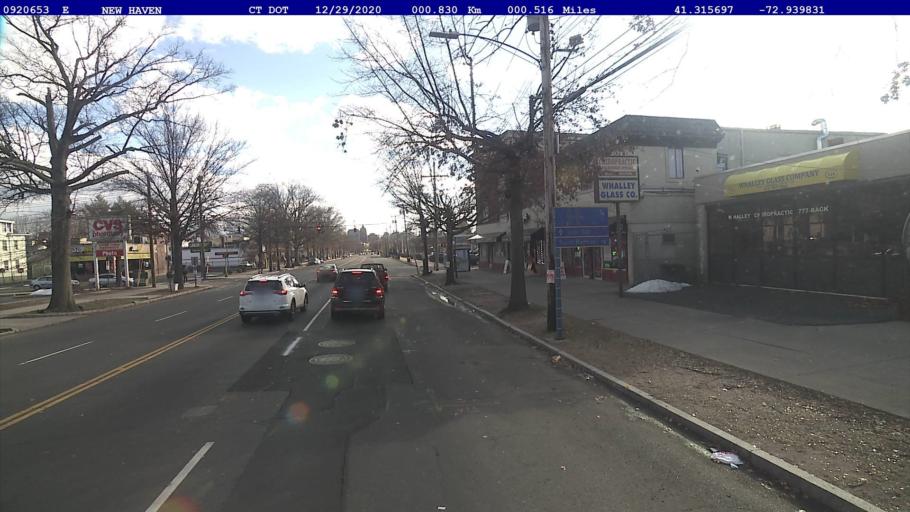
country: US
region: Connecticut
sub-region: New Haven County
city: New Haven
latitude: 41.3157
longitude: -72.9398
